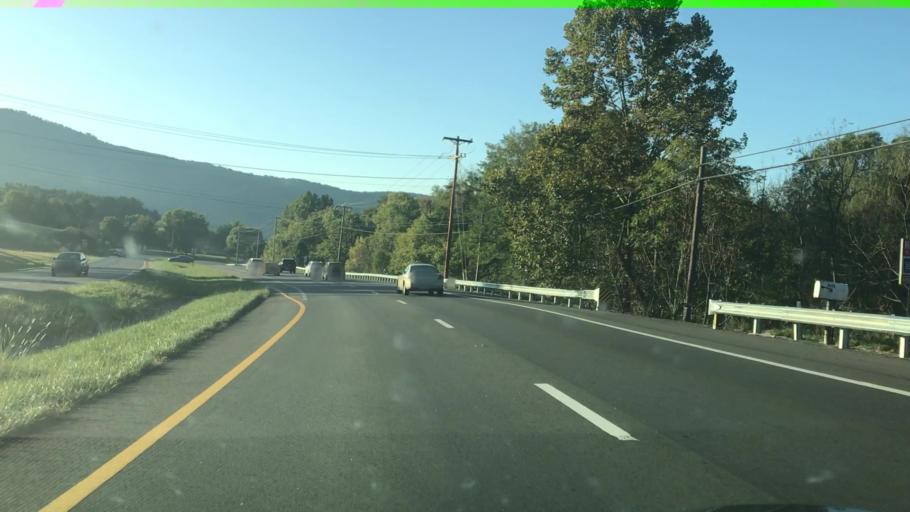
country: US
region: Virginia
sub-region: Botetourt County
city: Laymantown
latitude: 37.3344
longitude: -79.8748
